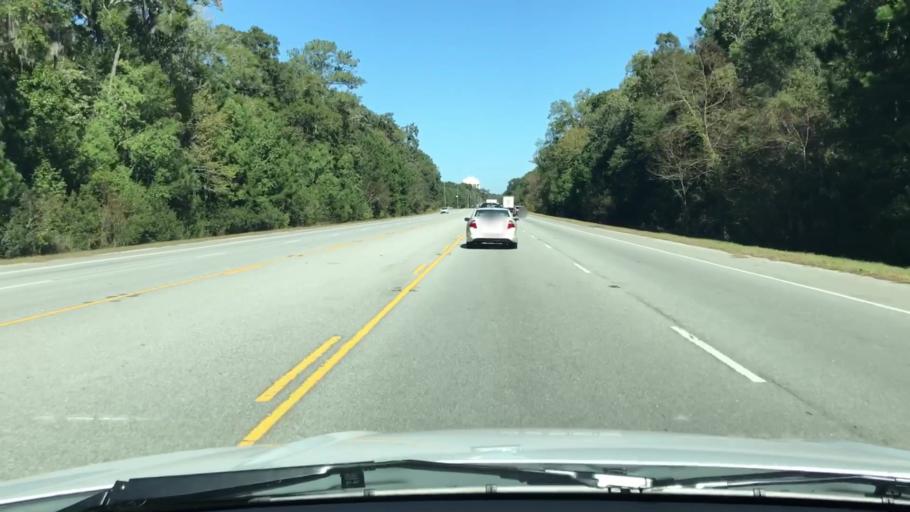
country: US
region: South Carolina
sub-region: Beaufort County
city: Shell Point
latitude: 32.4051
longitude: -80.7573
